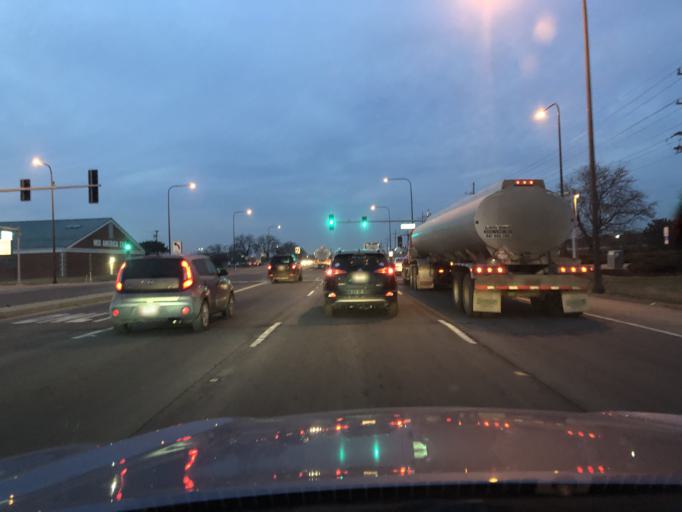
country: US
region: Illinois
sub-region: Cook County
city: Elk Grove Village
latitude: 42.0156
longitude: -87.9598
